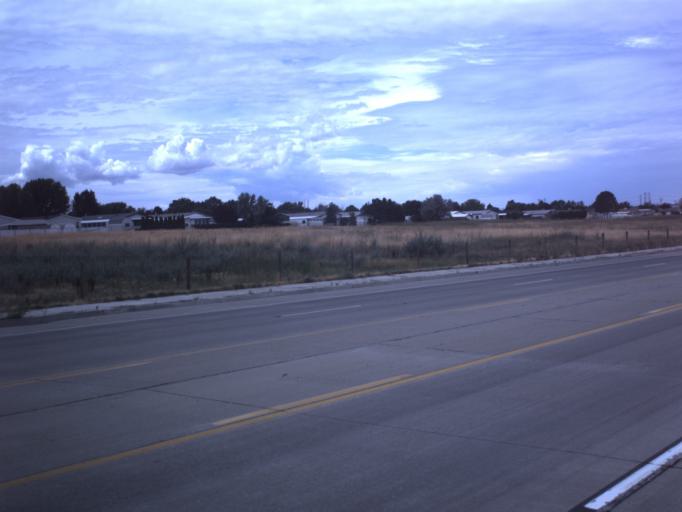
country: US
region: Utah
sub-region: Weber County
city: West Haven
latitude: 41.1975
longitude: -112.0357
